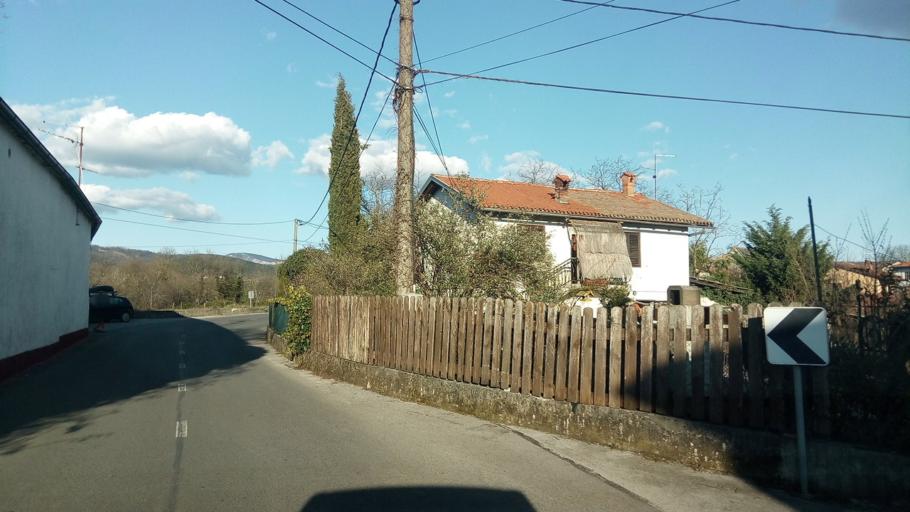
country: SI
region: Sezana
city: Sezana
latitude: 45.7614
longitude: 13.9054
